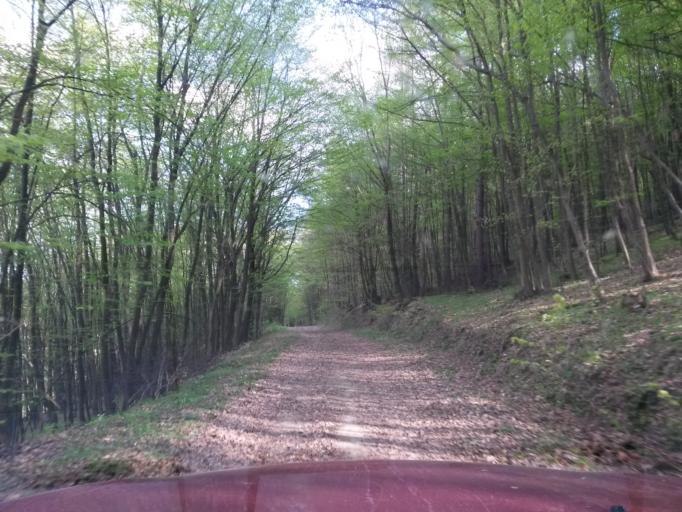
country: SK
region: Presovsky
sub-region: Okres Presov
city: Presov
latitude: 48.9499
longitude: 21.1576
